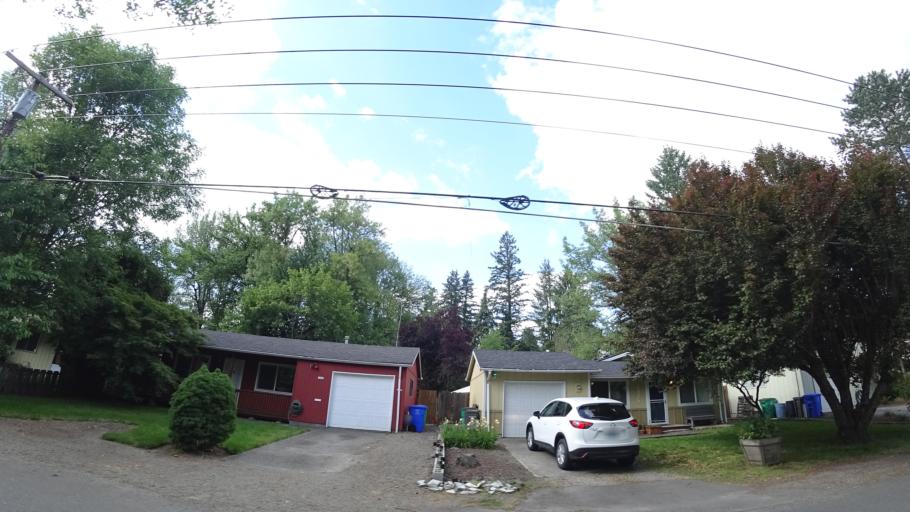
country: US
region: Oregon
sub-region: Washington County
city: Garden Home-Whitford
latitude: 45.4653
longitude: -122.7109
